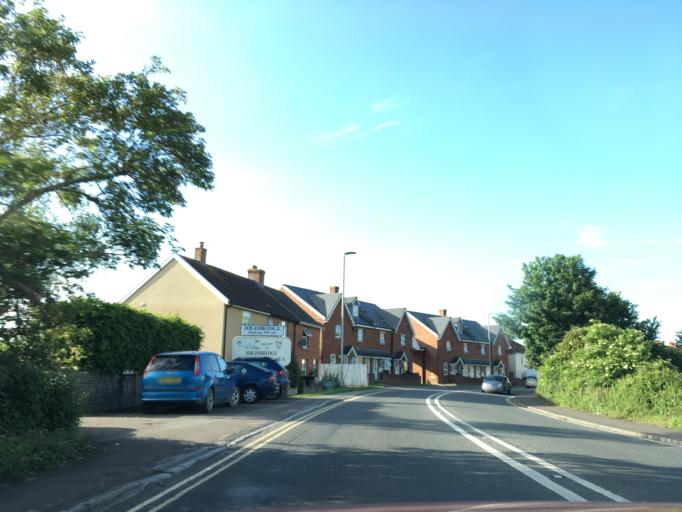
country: GB
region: England
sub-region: Somerset
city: Highbridge
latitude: 51.2168
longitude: -2.9818
